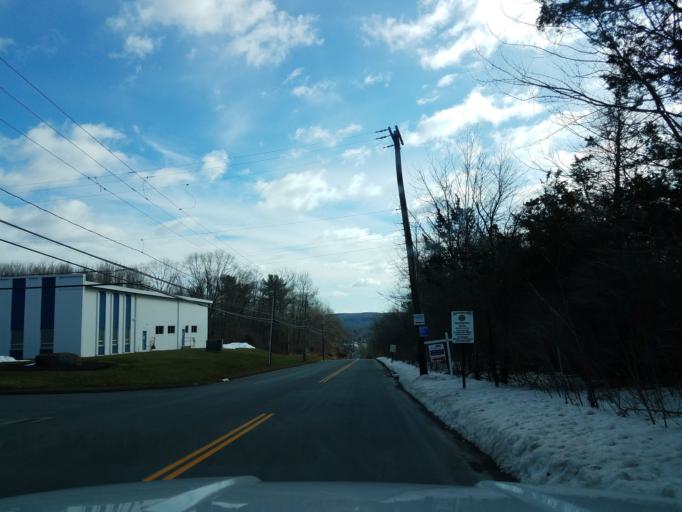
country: US
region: Connecticut
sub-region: Hartford County
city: Plainville
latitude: 41.6395
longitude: -72.8897
